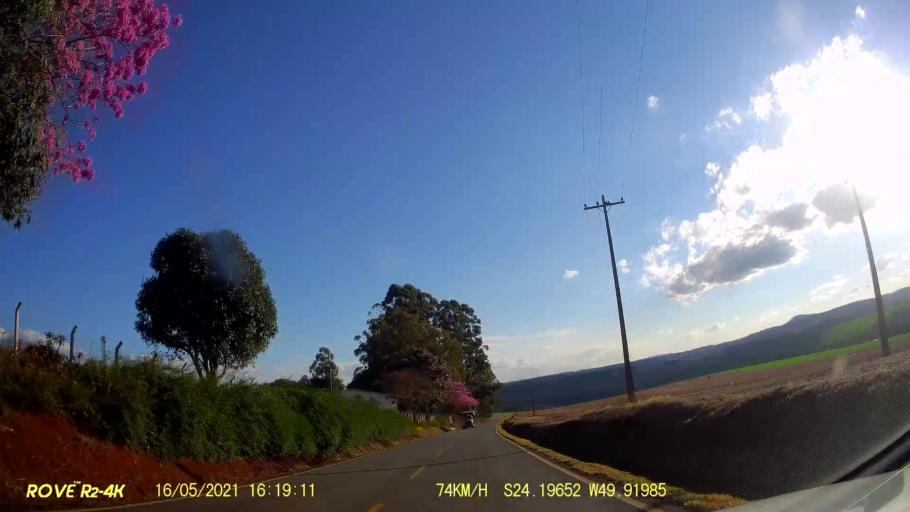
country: BR
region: Parana
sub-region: Jaguariaiva
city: Jaguariaiva
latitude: -24.1965
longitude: -49.9199
